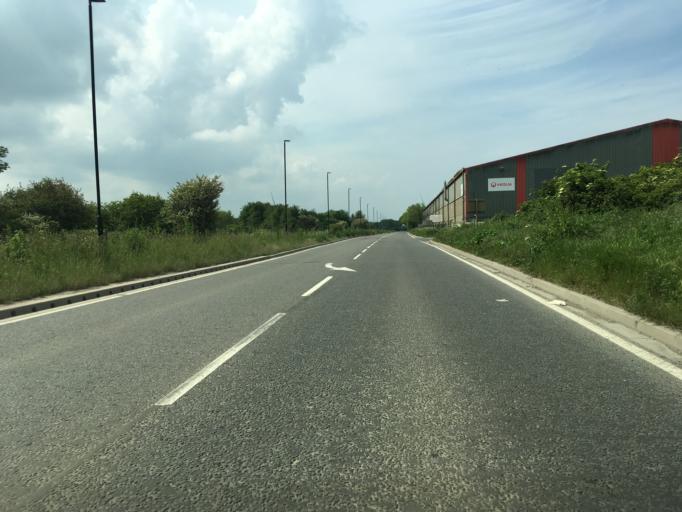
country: GB
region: England
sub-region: South Gloucestershire
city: Severn Beach
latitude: 51.5305
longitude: -2.6738
